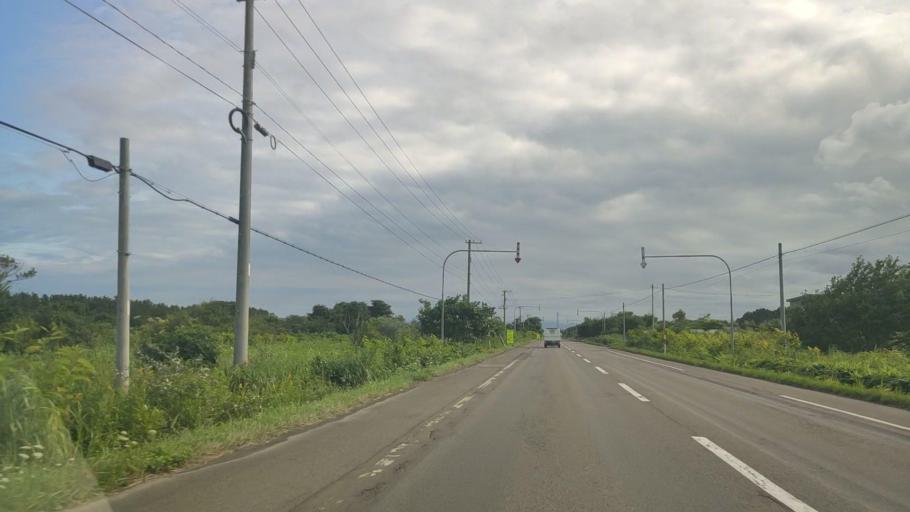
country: JP
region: Hokkaido
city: Niseko Town
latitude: 42.4656
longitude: 140.3397
